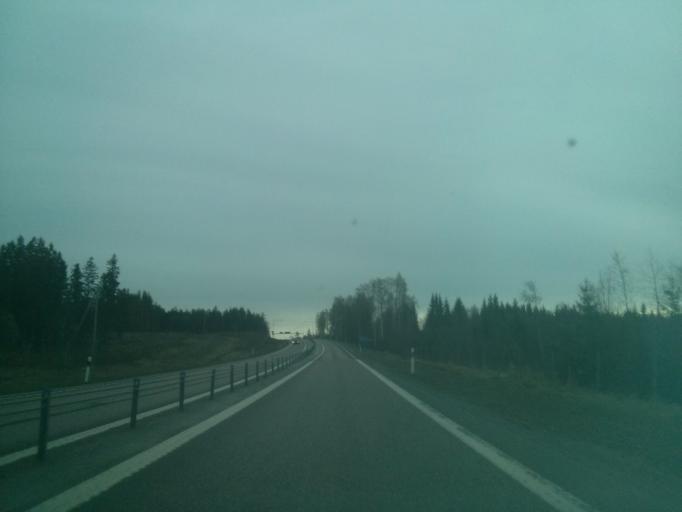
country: SE
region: Vaesternorrland
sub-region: Haernoesands Kommun
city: Haernoesand
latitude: 62.5960
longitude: 17.8040
